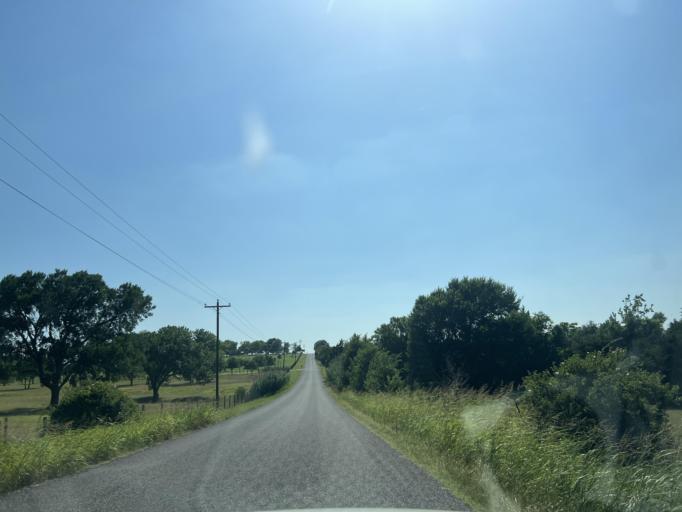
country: US
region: Texas
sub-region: Washington County
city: Brenham
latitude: 30.1623
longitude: -96.3286
